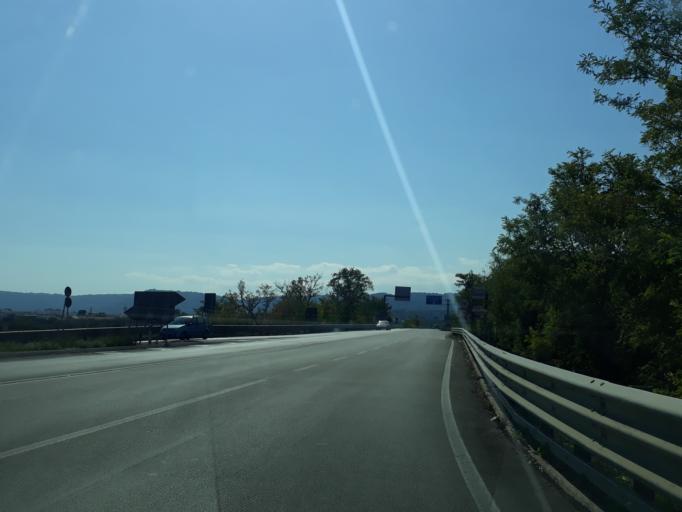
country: IT
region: Apulia
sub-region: Provincia di Brindisi
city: Fasano
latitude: 40.8498
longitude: 17.3569
